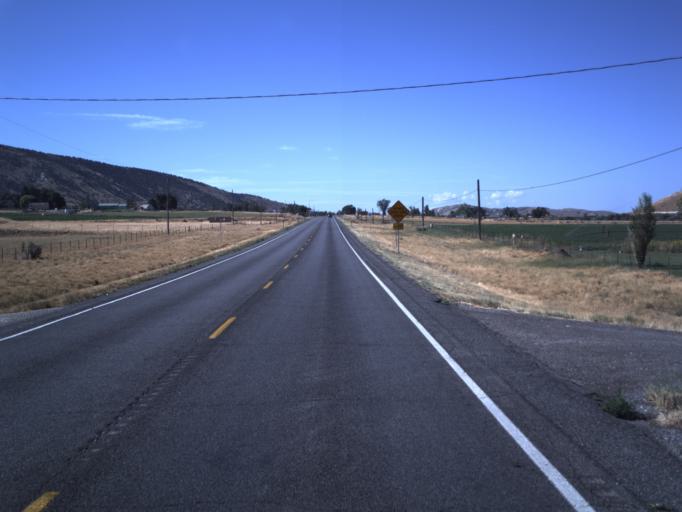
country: US
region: Utah
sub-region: Sanpete County
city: Manti
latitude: 39.2049
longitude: -111.6910
